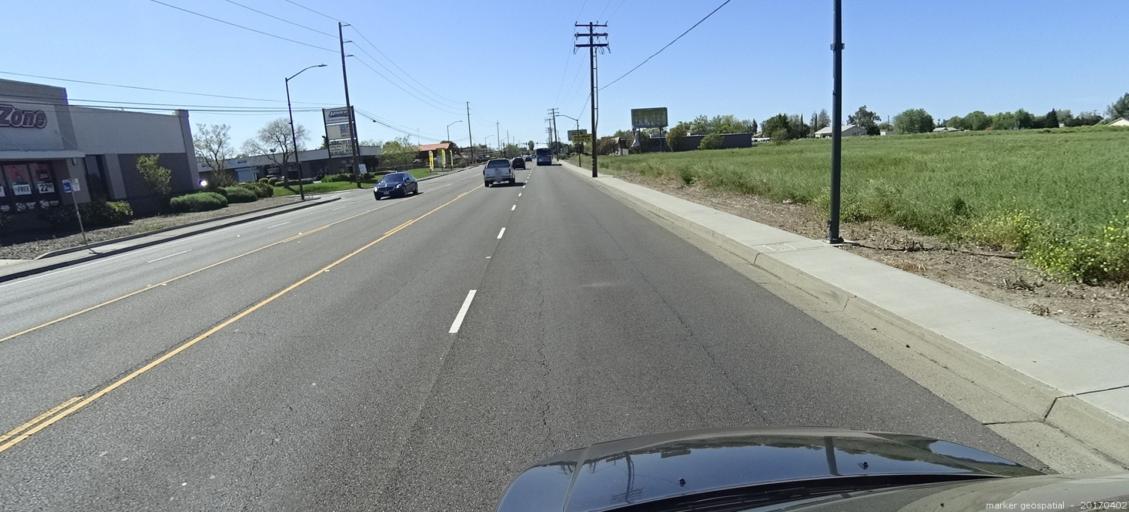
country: US
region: California
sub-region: Sacramento County
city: Parkway
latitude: 38.4958
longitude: -121.4758
